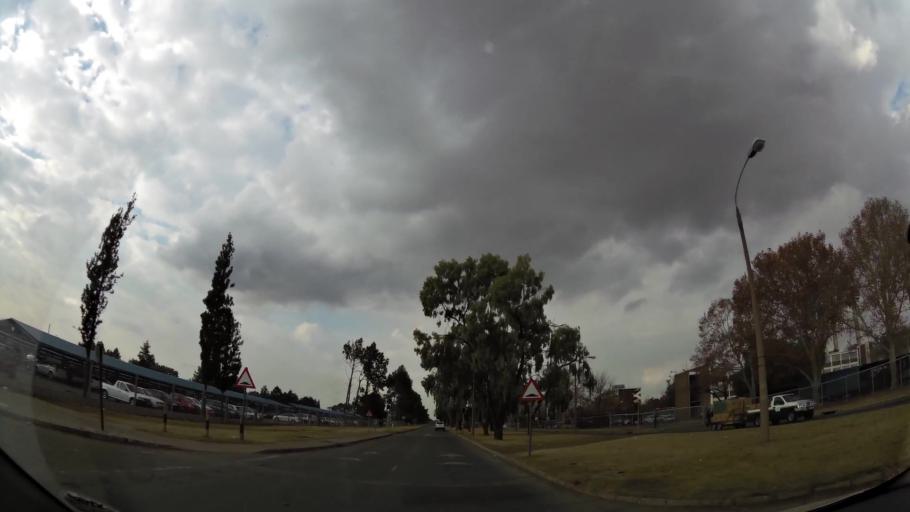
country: ZA
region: Orange Free State
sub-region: Fezile Dabi District Municipality
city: Sasolburg
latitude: -26.8201
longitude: 27.8371
